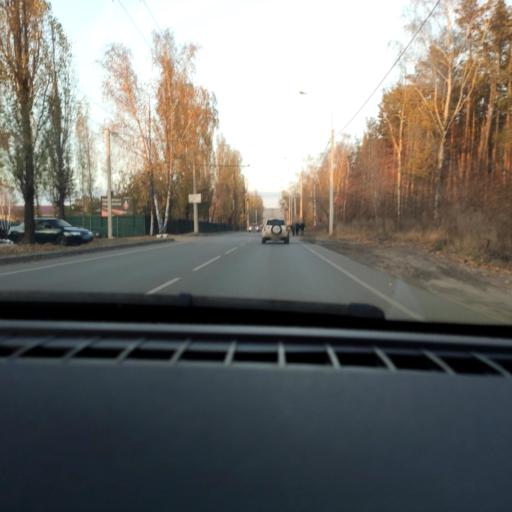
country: RU
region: Voronezj
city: Somovo
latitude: 51.7049
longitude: 39.2910
